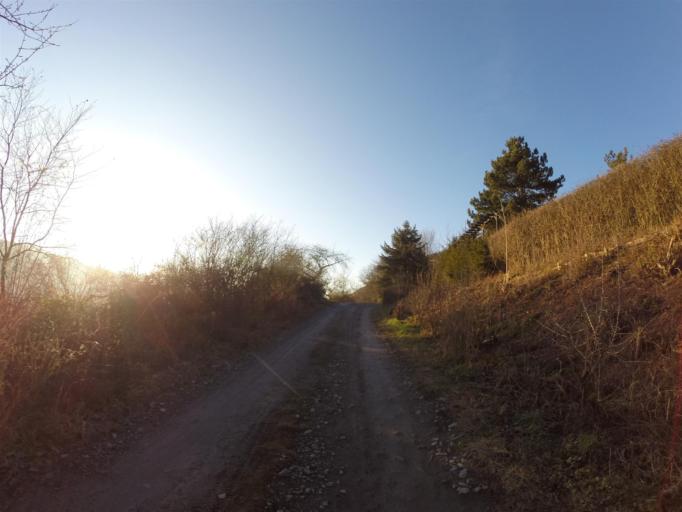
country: DE
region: Thuringia
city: Grosslobichau
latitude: 50.9361
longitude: 11.6509
